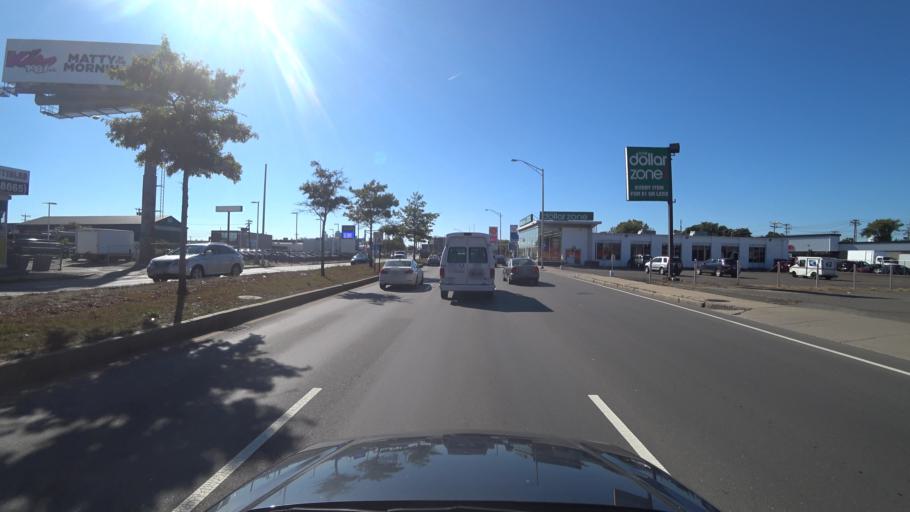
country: US
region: Massachusetts
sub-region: Essex County
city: Lynn
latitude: 42.4560
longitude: -70.9567
